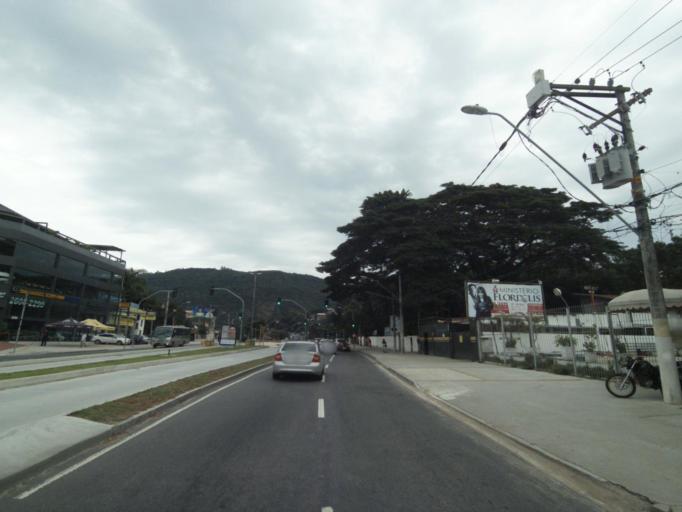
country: BR
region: Rio de Janeiro
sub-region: Niteroi
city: Niteroi
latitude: -22.9337
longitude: -43.0656
